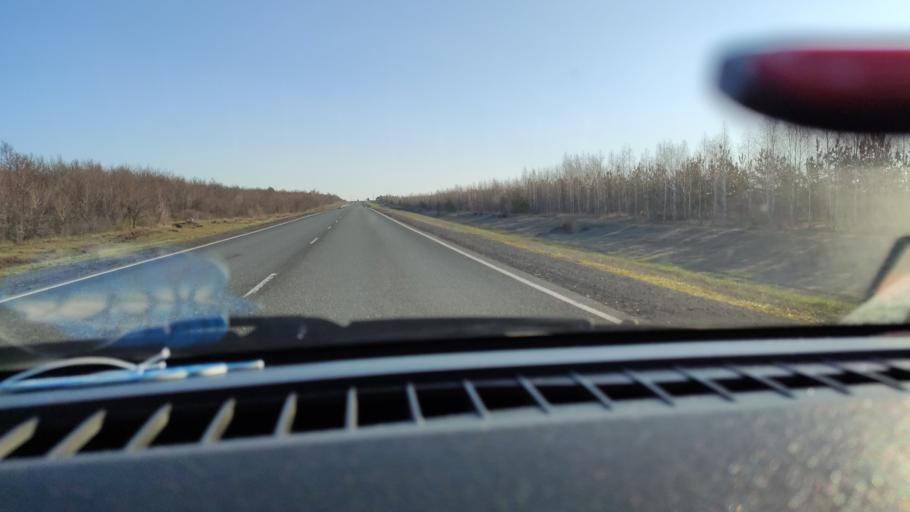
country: RU
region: Saratov
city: Balakovo
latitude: 52.1520
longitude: 47.8130
